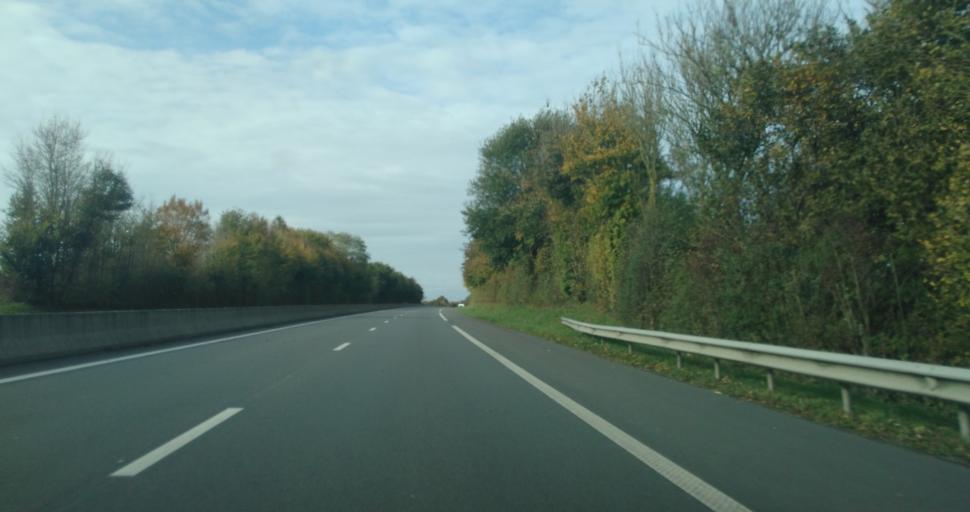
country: FR
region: Nord-Pas-de-Calais
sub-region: Departement du Pas-de-Calais
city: Saint-Pol-sur-Ternoise
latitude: 50.3637
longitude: 2.3857
